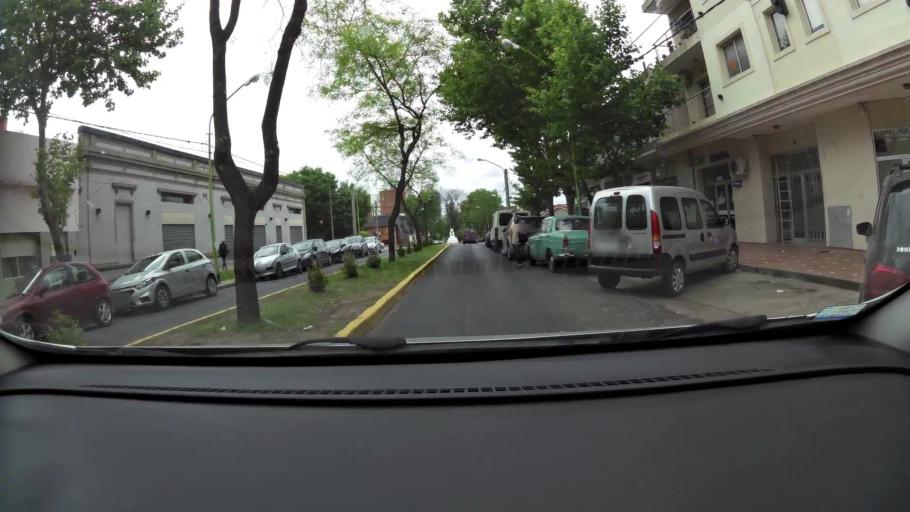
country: AR
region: Buenos Aires
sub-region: Partido de Campana
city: Campana
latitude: -34.1616
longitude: -58.9609
